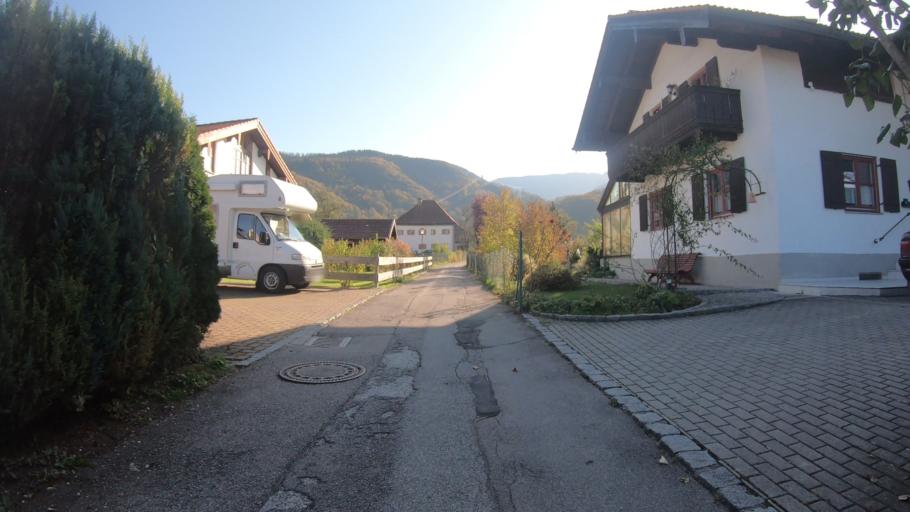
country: DE
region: Bavaria
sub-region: Upper Bavaria
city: Bergen
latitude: 47.8033
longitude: 12.5891
